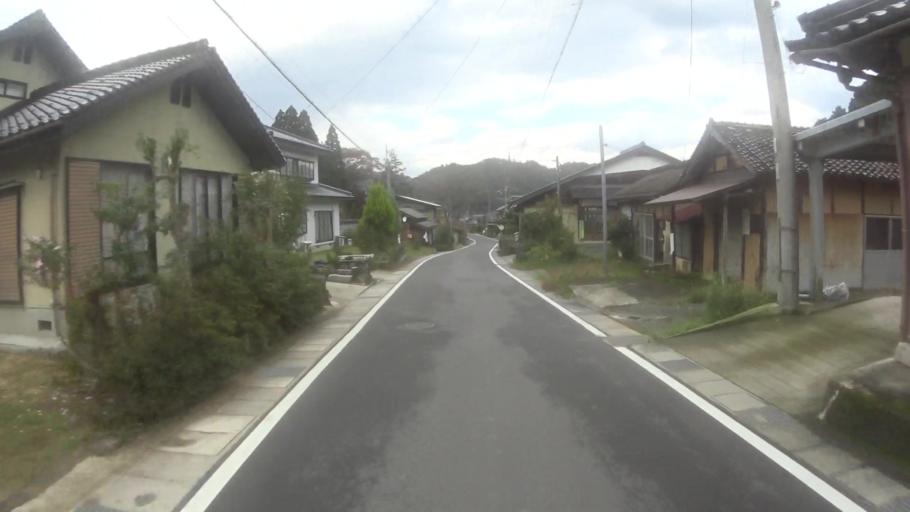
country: JP
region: Kyoto
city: Miyazu
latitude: 35.5212
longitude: 135.1255
